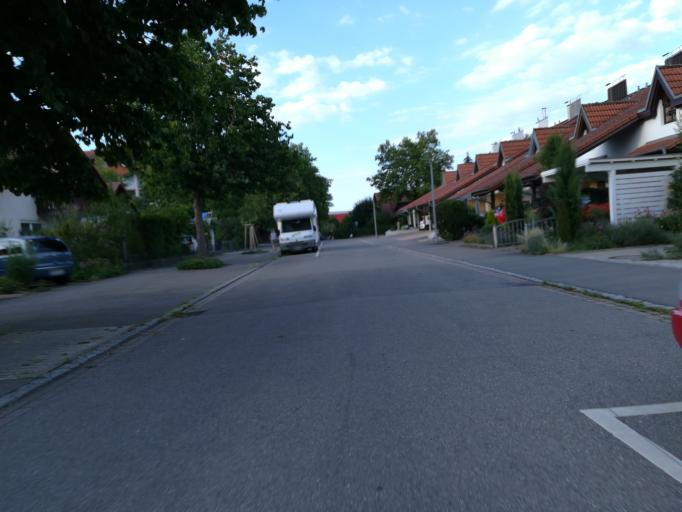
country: DE
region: Baden-Wuerttemberg
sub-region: Freiburg Region
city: Singen
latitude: 47.7568
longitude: 8.8207
